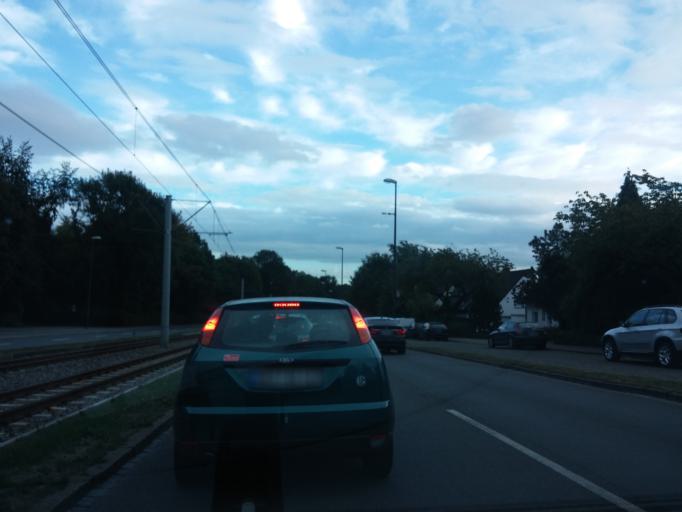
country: DE
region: North Rhine-Westphalia
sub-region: Regierungsbezirk Munster
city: Gladbeck
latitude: 51.5683
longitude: 7.0566
